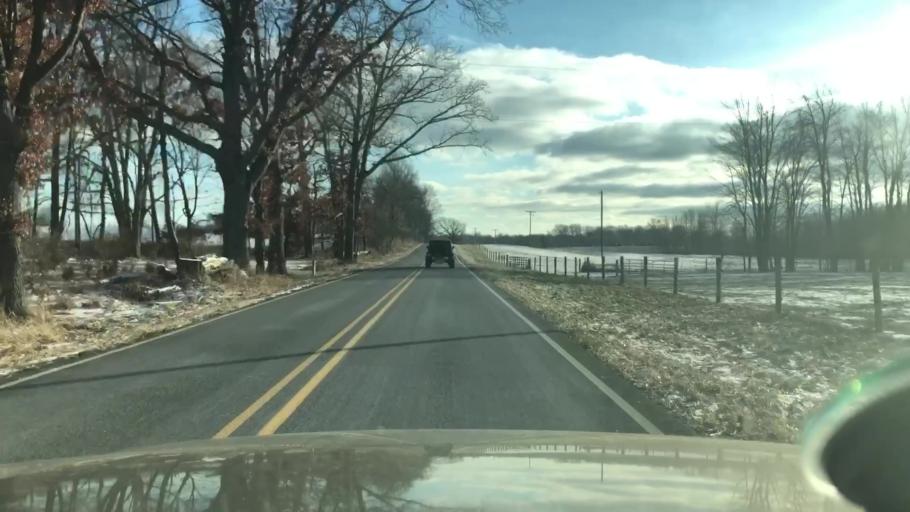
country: US
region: Michigan
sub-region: Jackson County
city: Vandercook Lake
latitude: 42.1027
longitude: -84.4511
